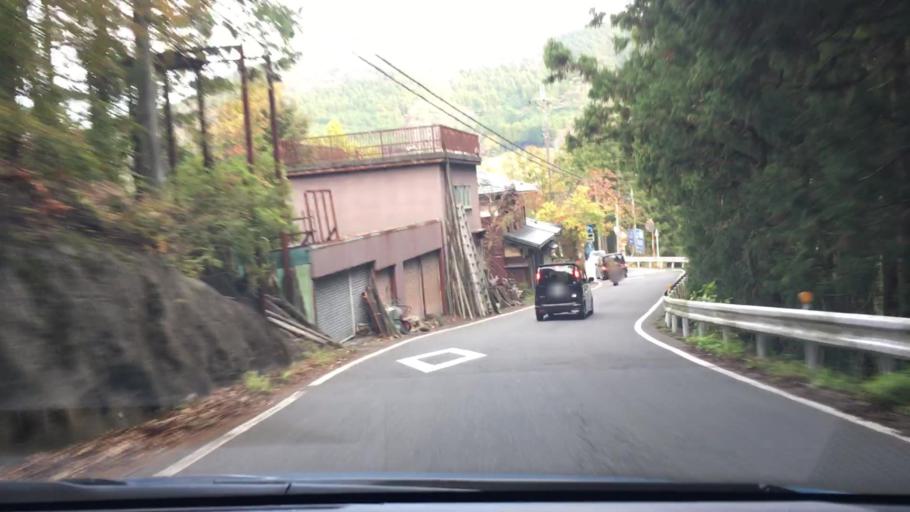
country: JP
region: Yamanashi
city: Uenohara
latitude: 35.5618
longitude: 139.1474
